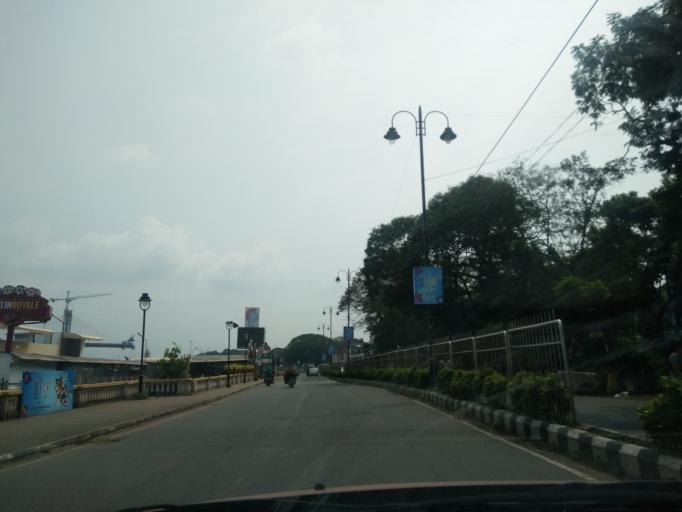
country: IN
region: Goa
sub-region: North Goa
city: Panaji
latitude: 15.5007
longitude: 73.8308
